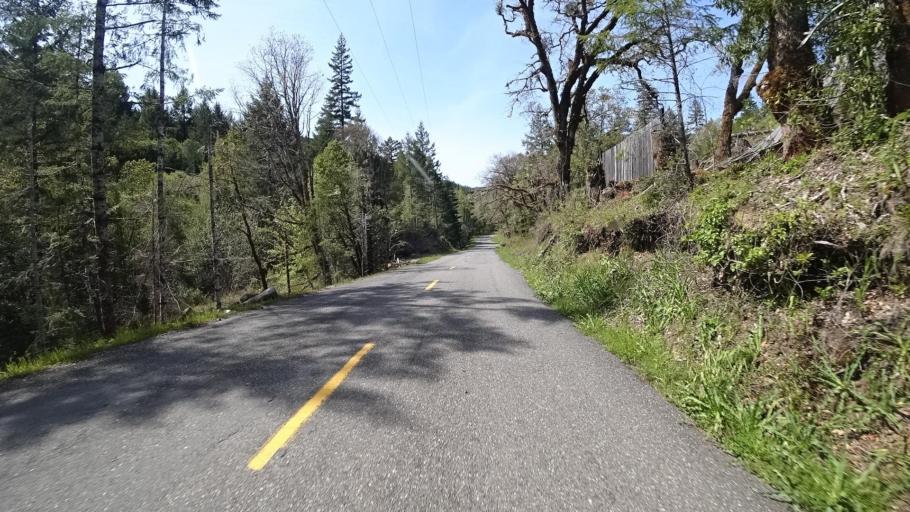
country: US
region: California
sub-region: Humboldt County
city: Redway
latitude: 40.3416
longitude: -123.7067
